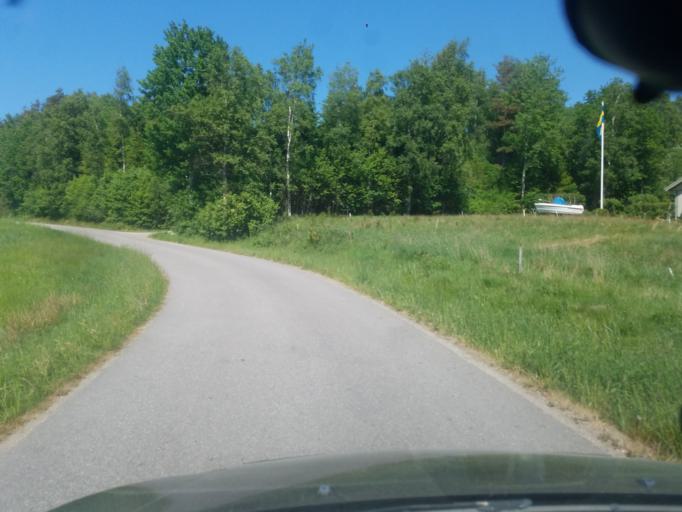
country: SE
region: Vaestra Goetaland
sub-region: Orust
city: Henan
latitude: 58.2763
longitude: 11.5772
